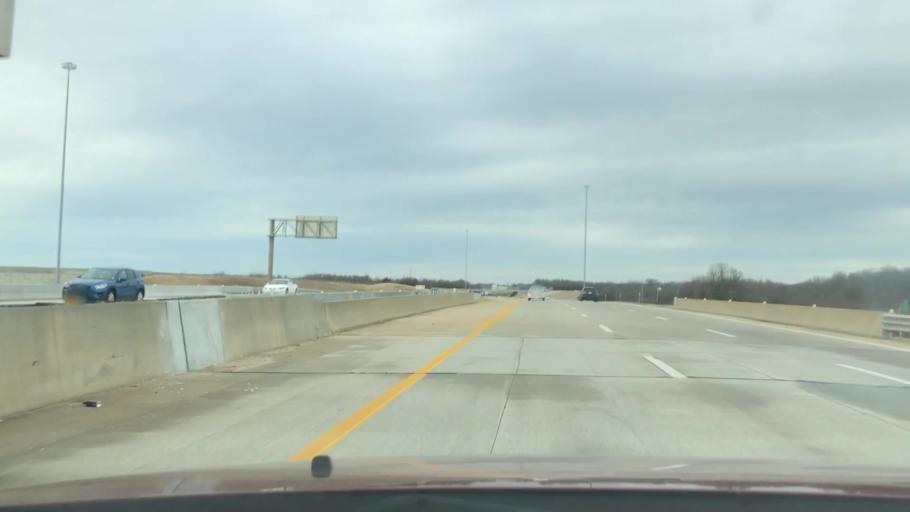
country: US
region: Missouri
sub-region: Greene County
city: Springfield
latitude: 37.2499
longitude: -93.2244
